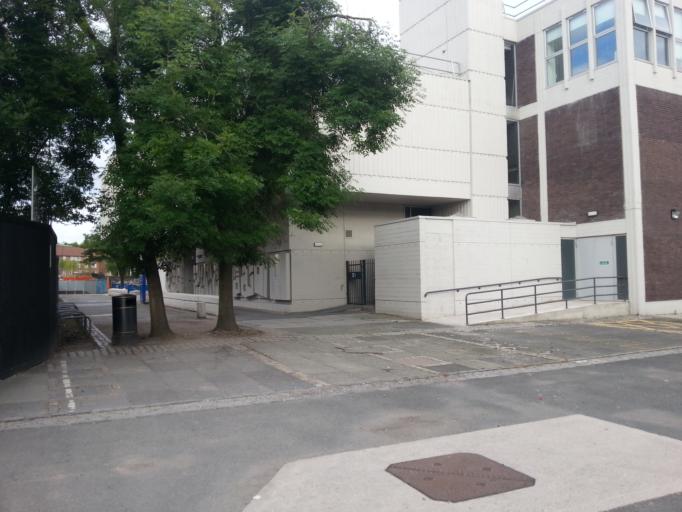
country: GB
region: England
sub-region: Liverpool
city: Liverpool
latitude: 53.4054
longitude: -2.9637
